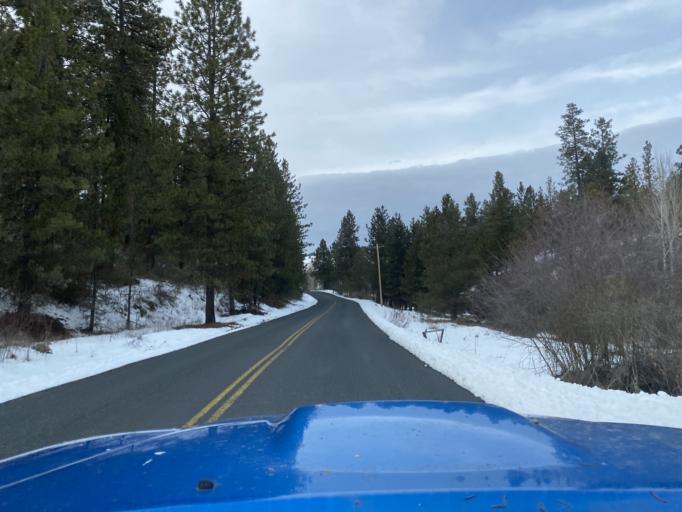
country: US
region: Idaho
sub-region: Latah County
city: Moscow
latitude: 46.6890
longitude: -116.9098
